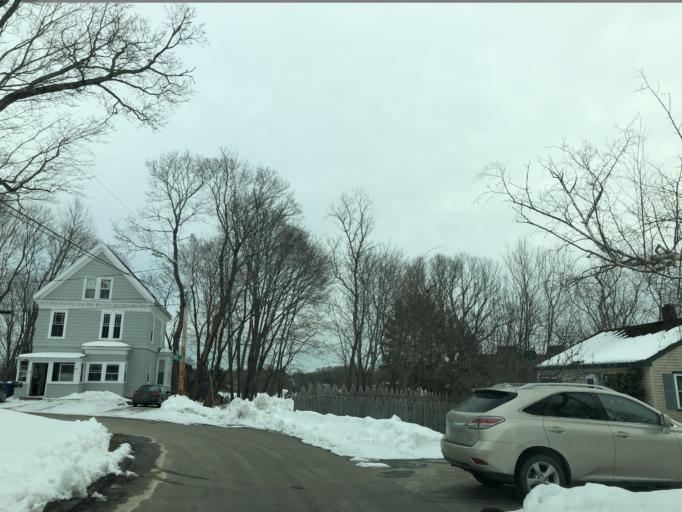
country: US
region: Maine
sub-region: Cumberland County
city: Westbrook
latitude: 43.6806
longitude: -70.3670
